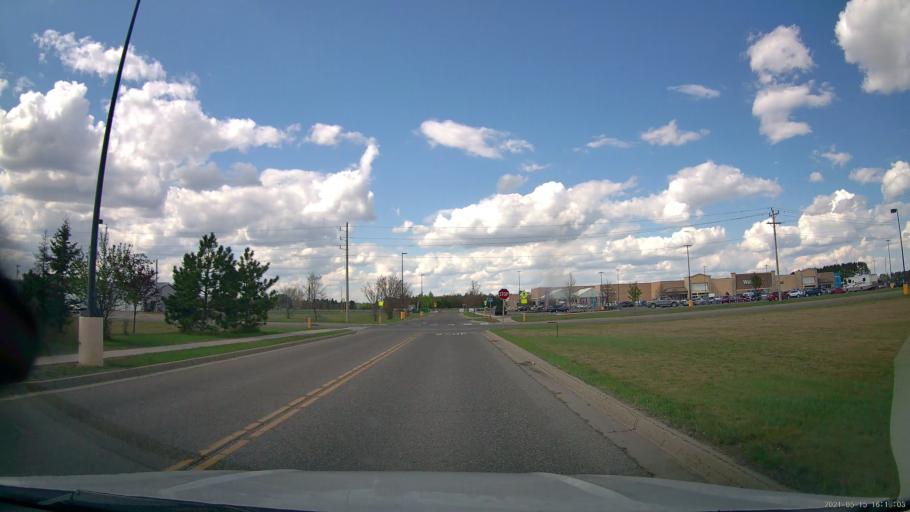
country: US
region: Minnesota
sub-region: Hubbard County
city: Park Rapids
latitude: 46.9232
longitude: -95.0352
